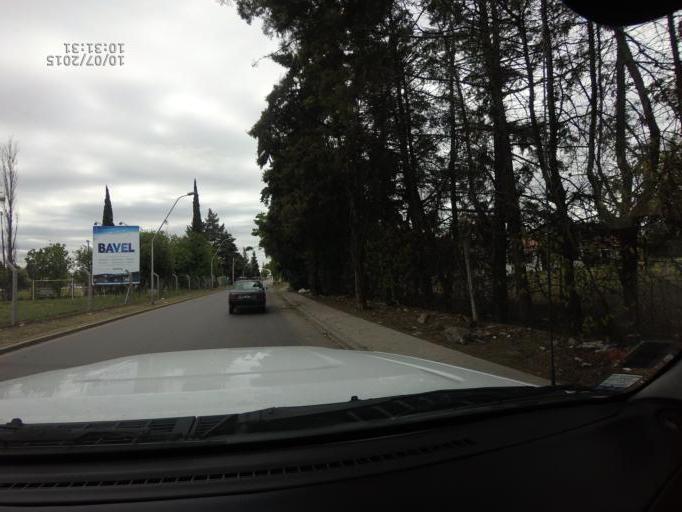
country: AR
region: Cordoba
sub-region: Departamento de Capital
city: Cordoba
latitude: -31.3559
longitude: -64.2371
